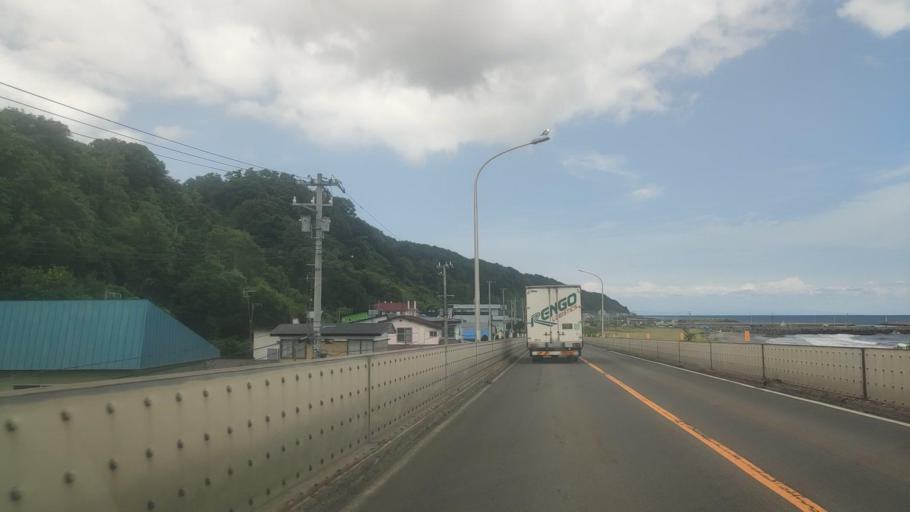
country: JP
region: Hokkaido
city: Nanae
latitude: 42.1290
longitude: 140.5141
